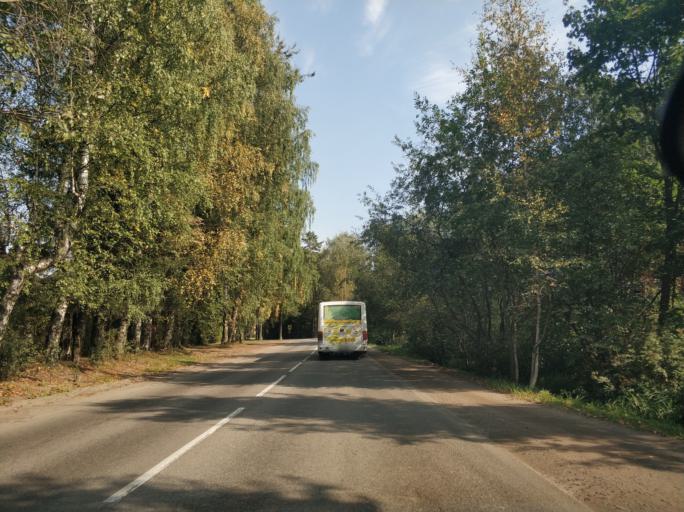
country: RU
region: Leningrad
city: Vsevolozhsk
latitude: 60.0101
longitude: 30.6175
